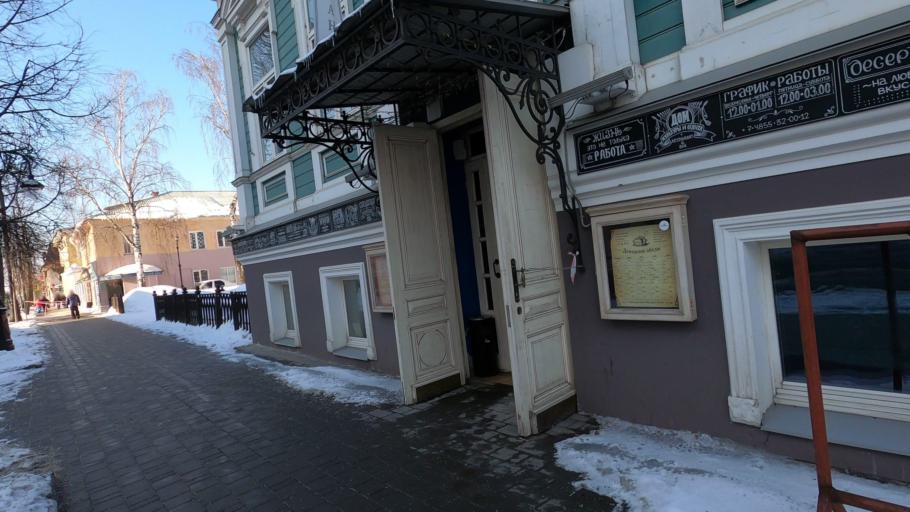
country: RU
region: Jaroslavl
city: Rybinsk
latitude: 58.0507
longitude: 38.8436
